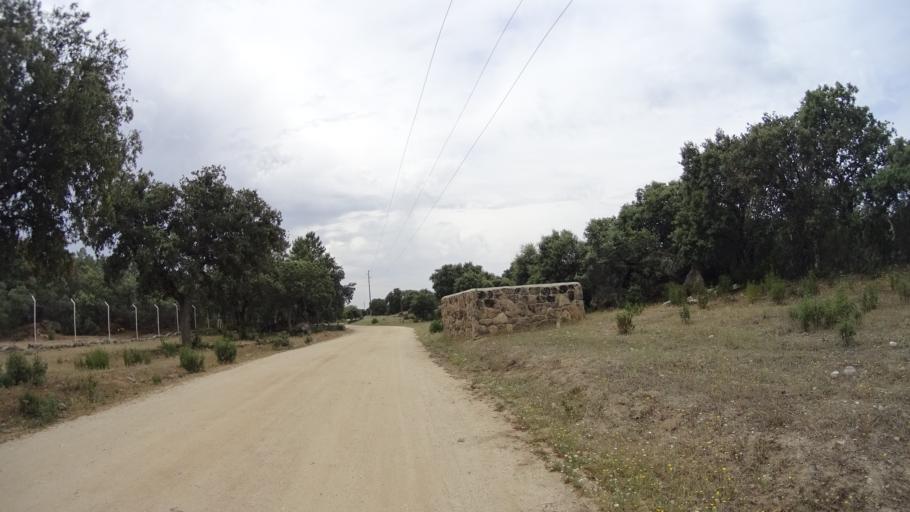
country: ES
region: Madrid
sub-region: Provincia de Madrid
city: Colmenarejo
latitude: 40.5590
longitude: -4.0363
